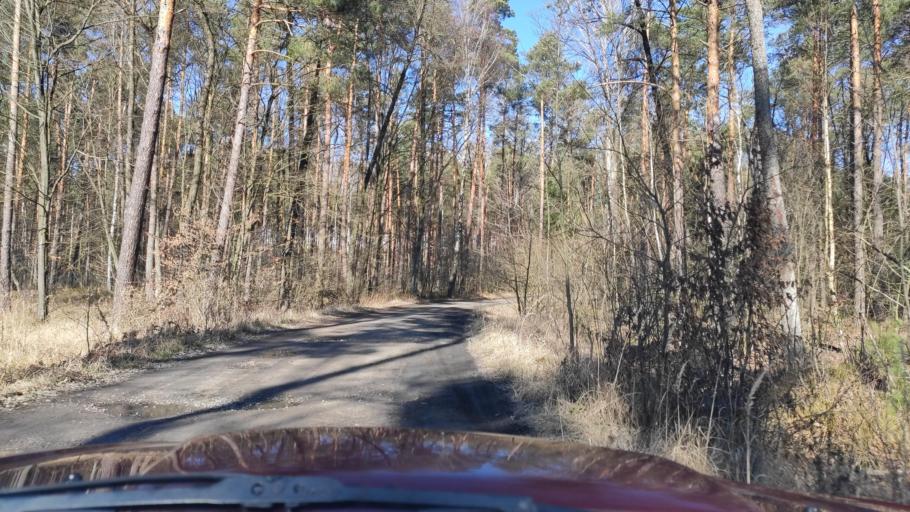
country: PL
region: Masovian Voivodeship
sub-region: Powiat kozienicki
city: Garbatka-Letnisko
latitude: 51.4452
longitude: 21.5352
